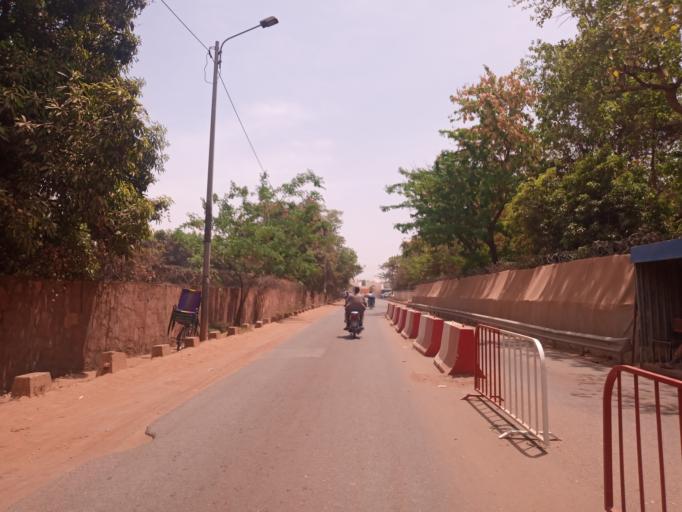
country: ML
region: Bamako
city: Bamako
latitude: 12.6368
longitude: -7.9939
